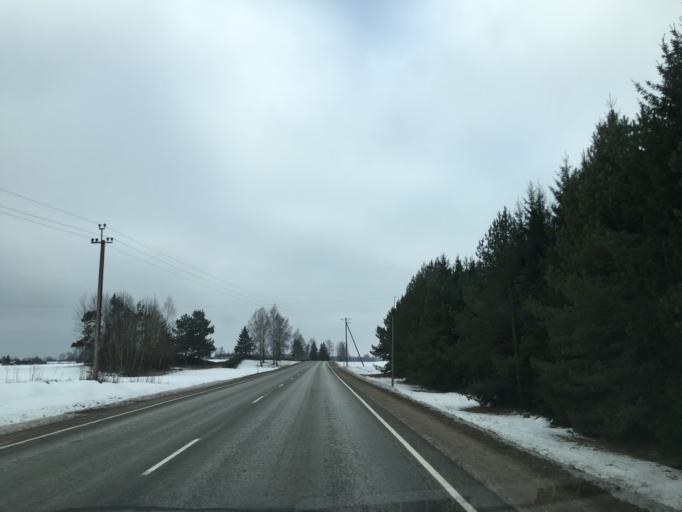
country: EE
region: Tartu
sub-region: Elva linn
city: Elva
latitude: 58.1285
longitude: 26.2444
